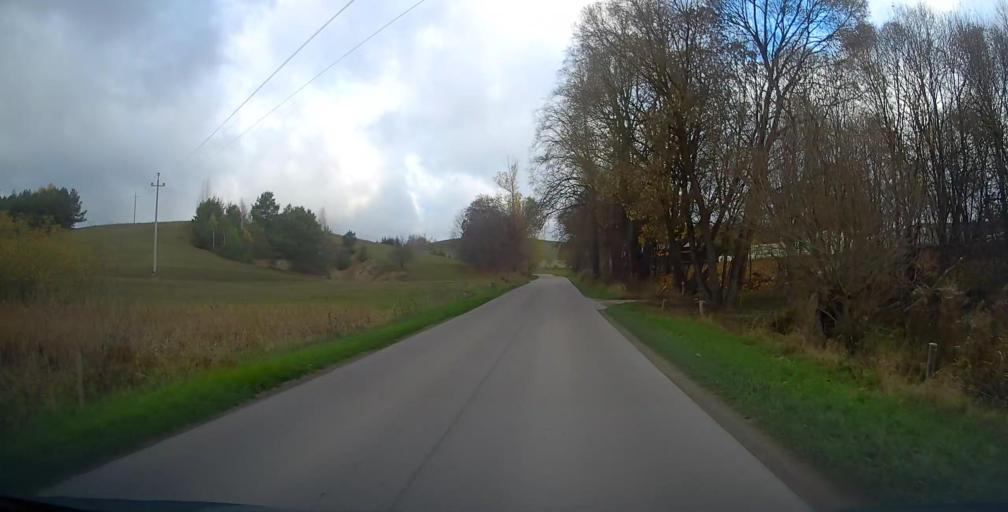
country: PL
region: Podlasie
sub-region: Suwalki
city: Suwalki
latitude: 54.2794
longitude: 22.9091
